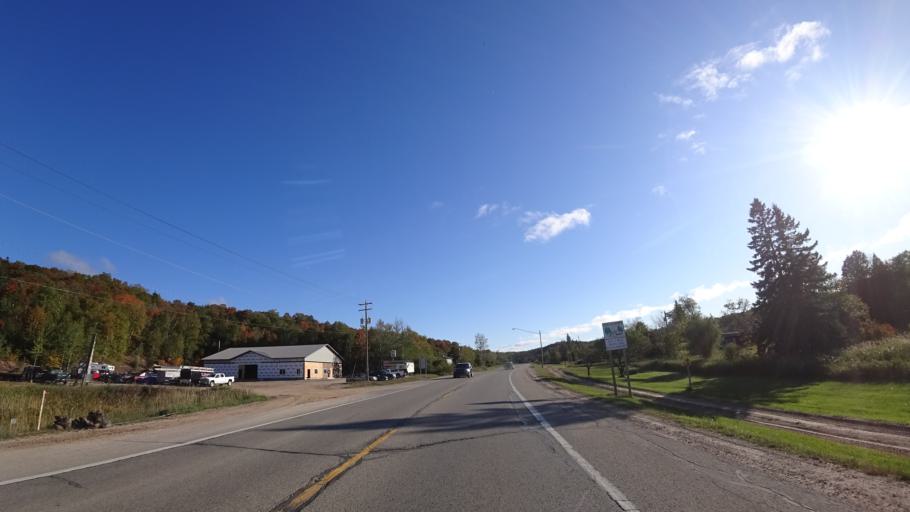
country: US
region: Michigan
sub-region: Alger County
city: Munising
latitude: 46.4013
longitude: -86.6477
